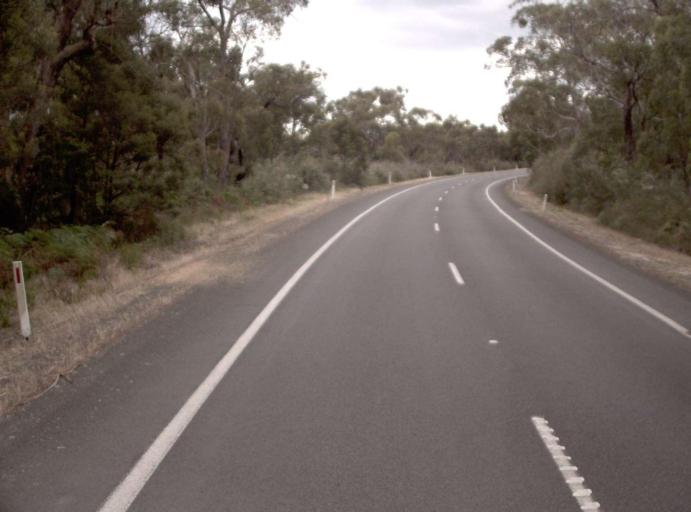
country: AU
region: Victoria
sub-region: Wellington
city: Sale
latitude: -38.2598
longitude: 147.0372
